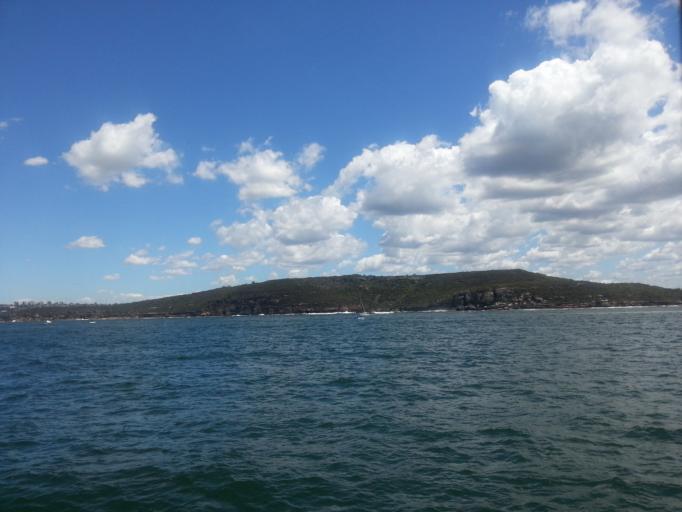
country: AU
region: New South Wales
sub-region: Manly Vale
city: Manly
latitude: -33.8175
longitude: 151.2795
